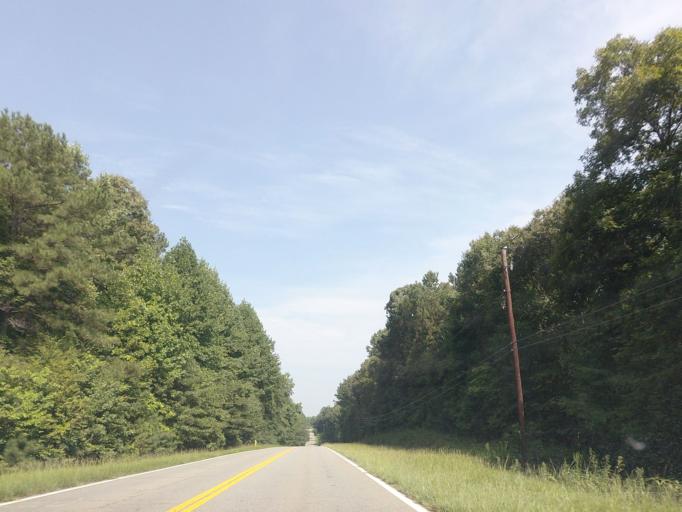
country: US
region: Georgia
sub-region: Bibb County
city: Macon
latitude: 32.9085
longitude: -83.6914
